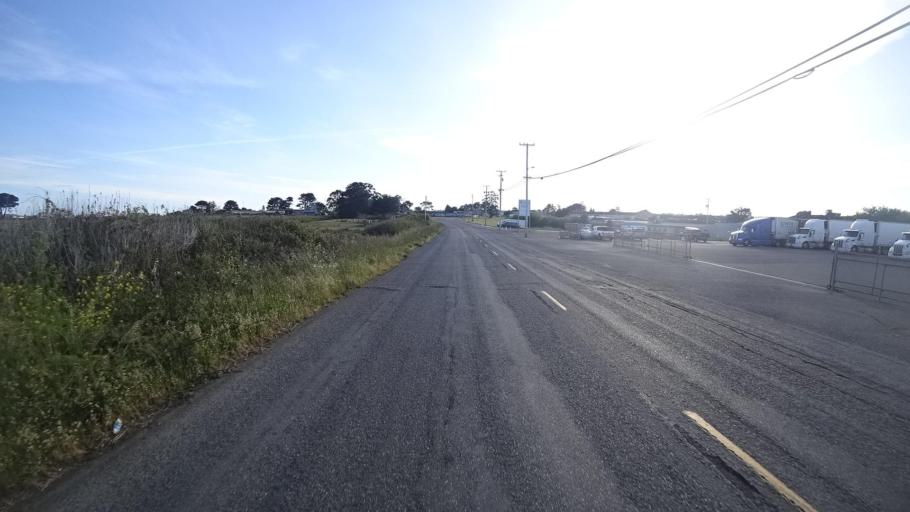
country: US
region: California
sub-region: Humboldt County
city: Humboldt Hill
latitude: 40.7402
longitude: -124.2023
